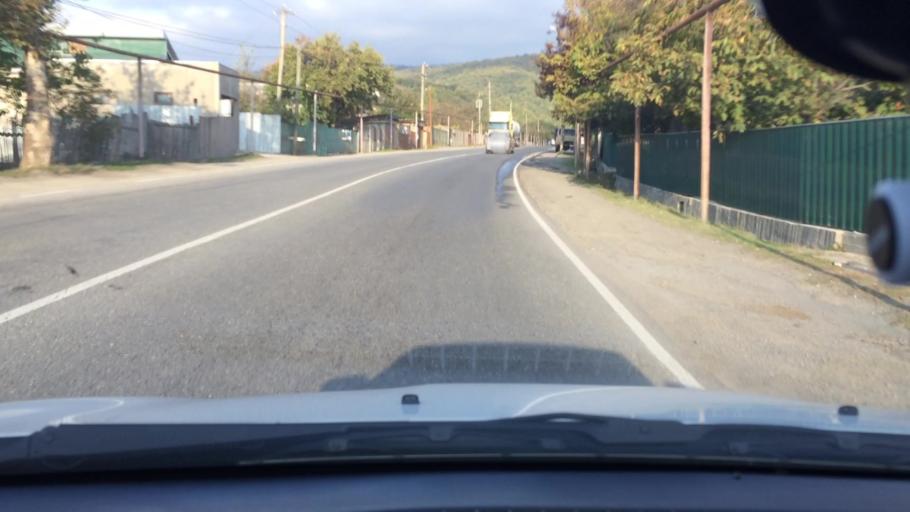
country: GE
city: Surami
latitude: 42.0292
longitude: 43.5297
